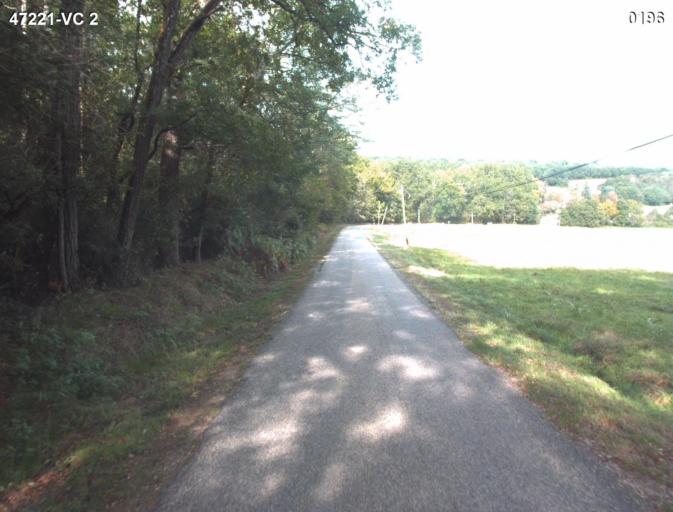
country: FR
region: Aquitaine
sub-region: Departement du Lot-et-Garonne
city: Mezin
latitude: 44.1082
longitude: 0.2367
